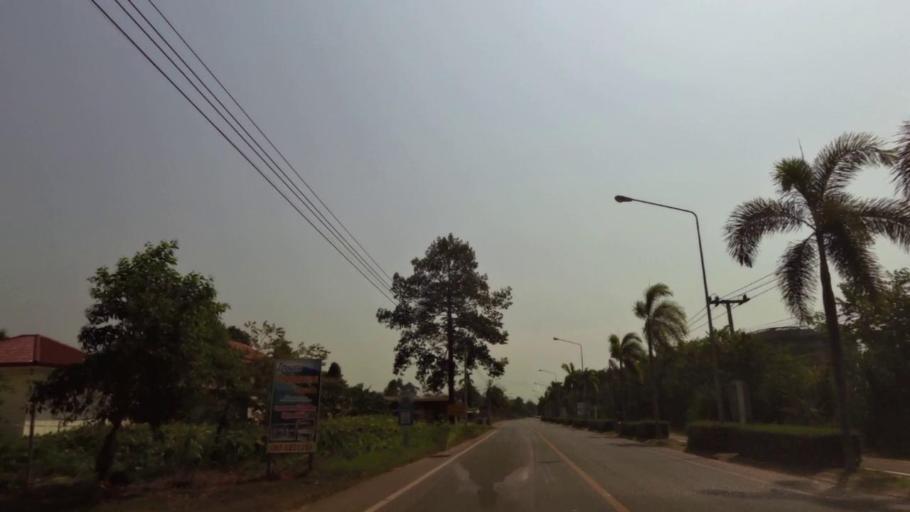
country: TH
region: Chanthaburi
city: Tha Mai
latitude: 12.5490
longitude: 101.9266
